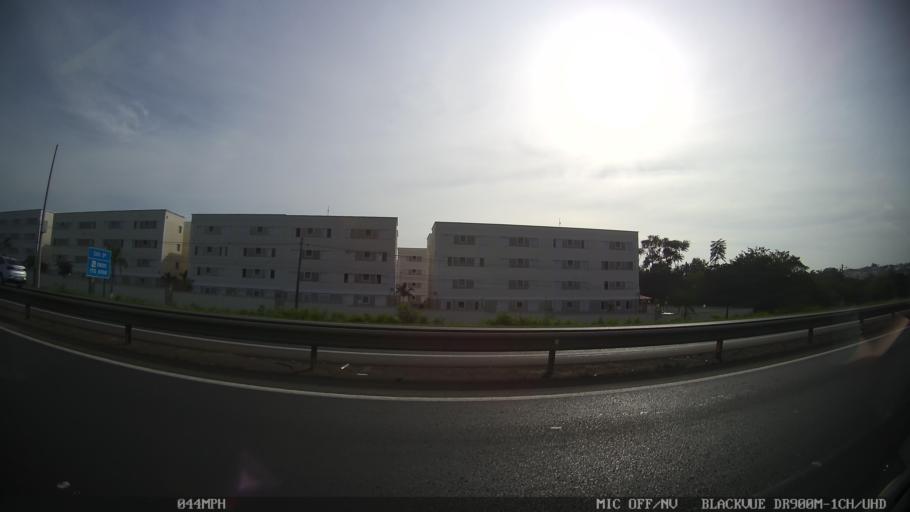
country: BR
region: Sao Paulo
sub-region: Piracicaba
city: Piracicaba
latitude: -22.6848
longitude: -47.6793
